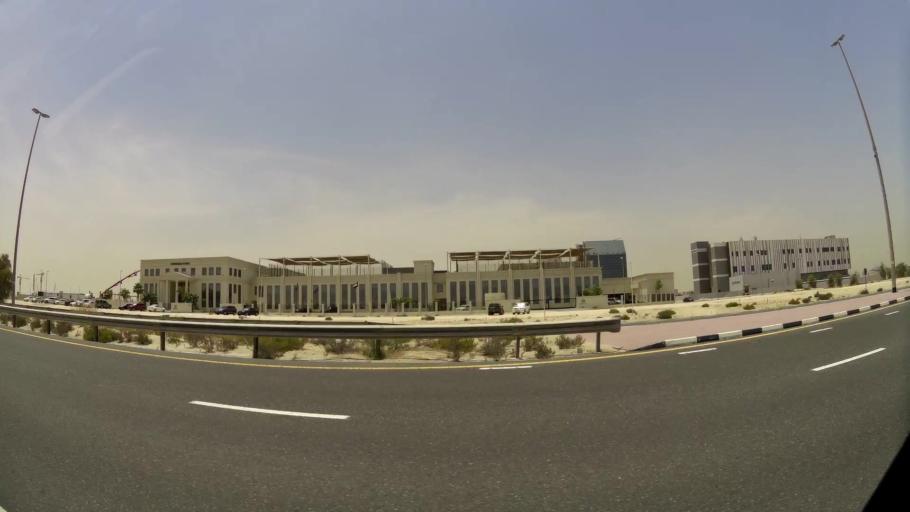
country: AE
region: Dubai
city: Dubai
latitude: 25.0809
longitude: 55.2420
